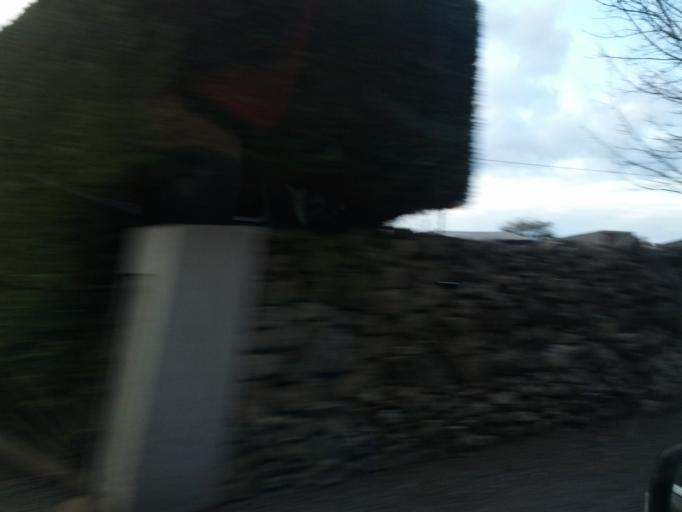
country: IE
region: Connaught
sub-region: County Galway
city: Athenry
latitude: 53.4155
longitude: -8.7518
